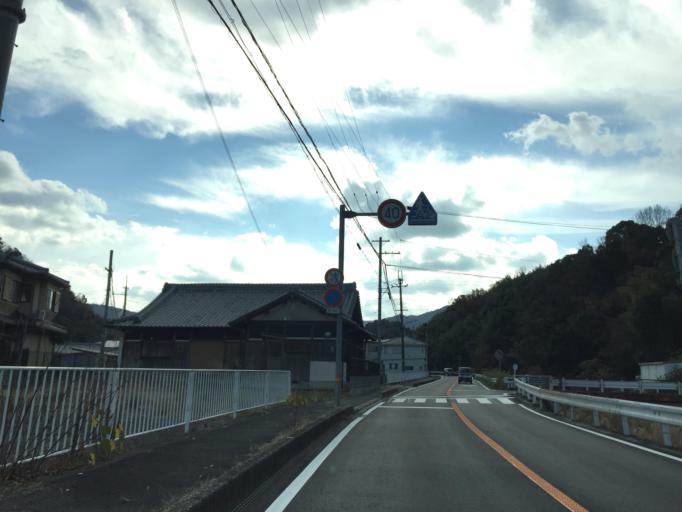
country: JP
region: Wakayama
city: Kainan
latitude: 34.1693
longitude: 135.2508
